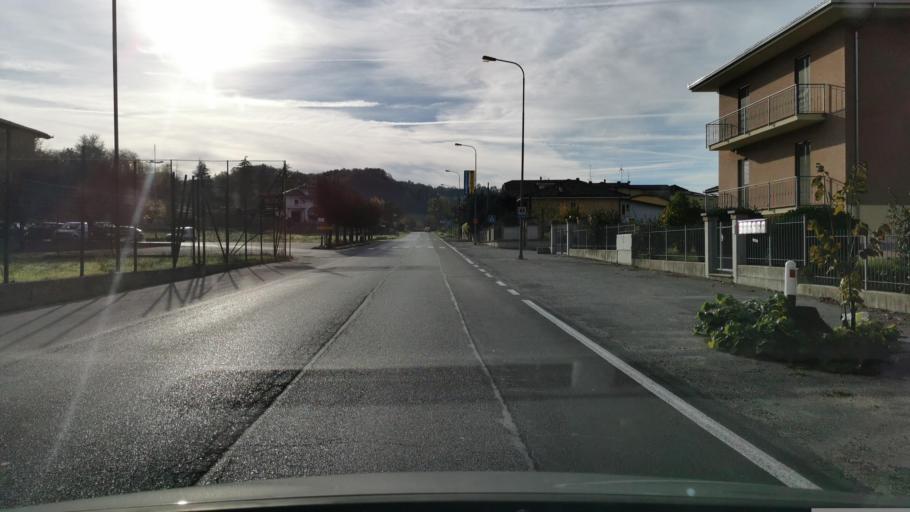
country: IT
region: Piedmont
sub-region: Provincia di Cuneo
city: Monchiero Borgonuovo
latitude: 44.5665
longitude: 7.9197
